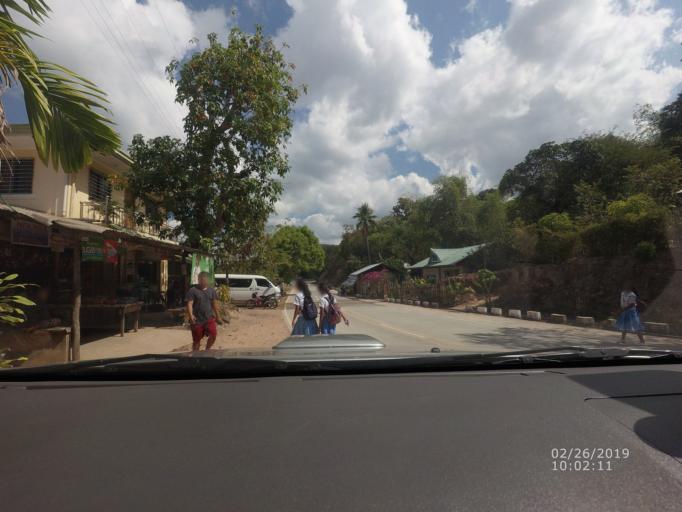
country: PH
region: Mimaropa
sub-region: Province of Palawan
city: Salvacion
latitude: 12.0528
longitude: 119.9719
